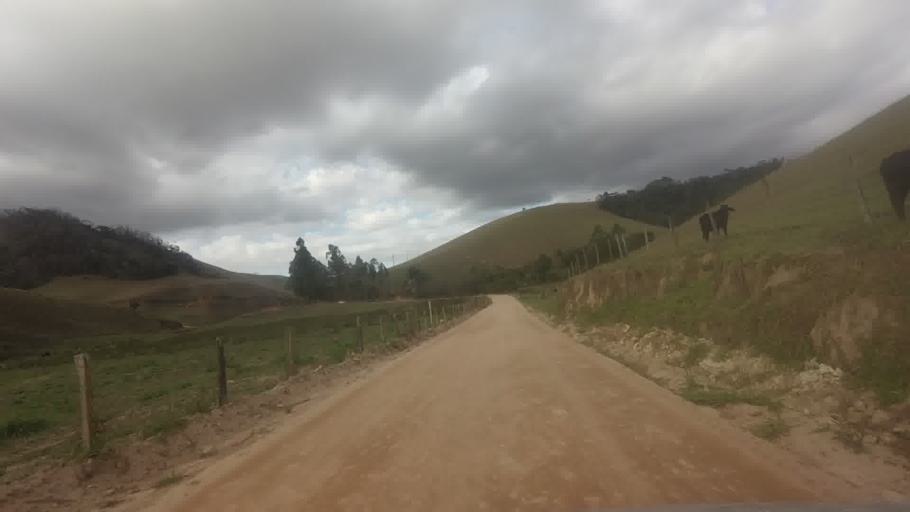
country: BR
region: Espirito Santo
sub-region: Mimoso Do Sul
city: Mimoso do Sul
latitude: -20.9576
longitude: -41.4317
